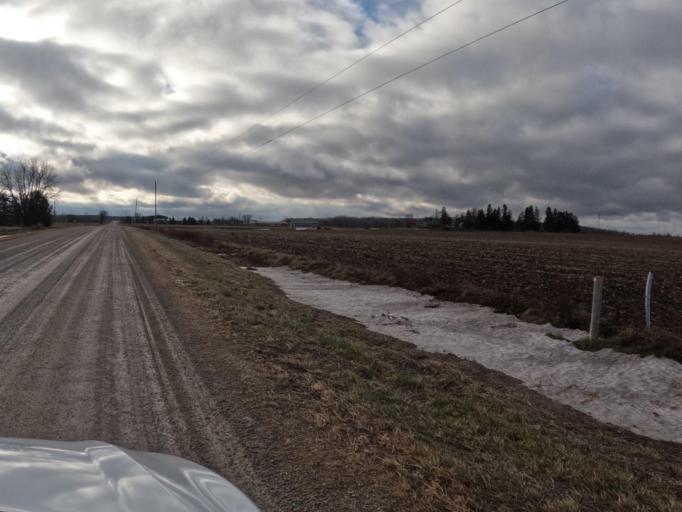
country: CA
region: Ontario
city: Shelburne
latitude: 43.8836
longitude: -80.3586
